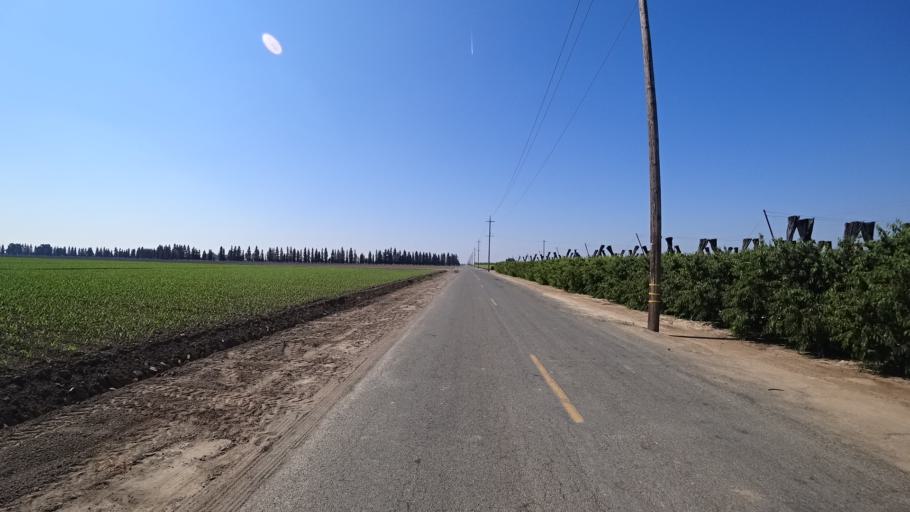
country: US
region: California
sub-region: Kings County
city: Lucerne
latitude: 36.4171
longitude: -119.5829
